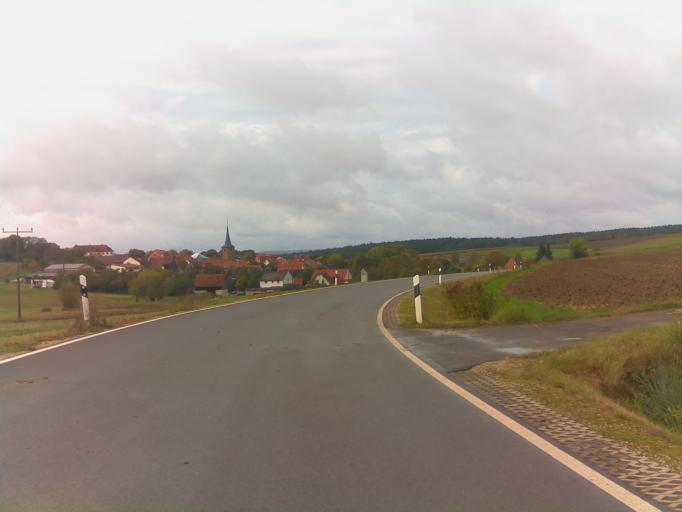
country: DE
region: Bavaria
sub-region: Upper Franconia
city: Zapfendorf
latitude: 50.0130
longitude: 10.9882
